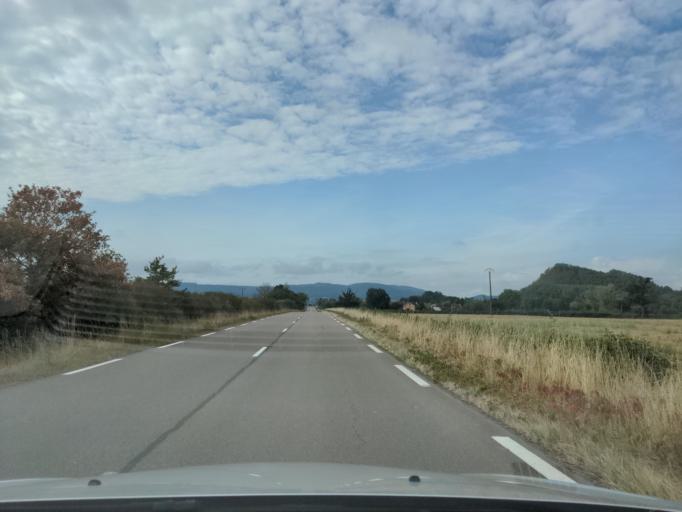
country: FR
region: Bourgogne
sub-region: Departement de Saone-et-Loire
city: Autun
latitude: 46.9933
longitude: 4.3165
